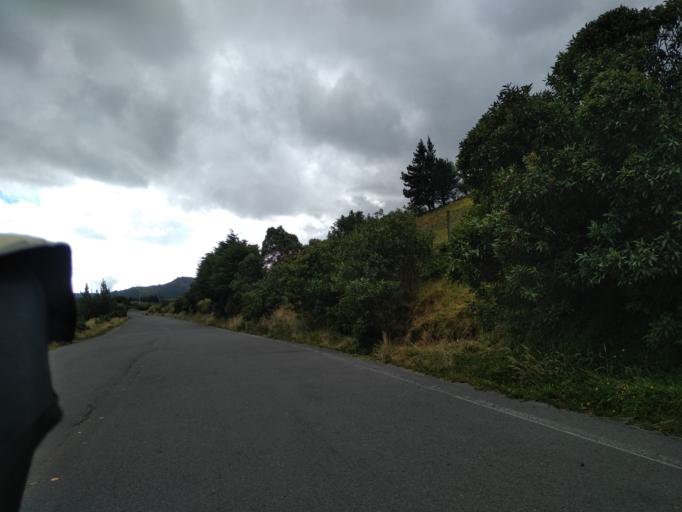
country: EC
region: Cotopaxi
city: Saquisili
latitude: -0.7202
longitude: -78.7621
